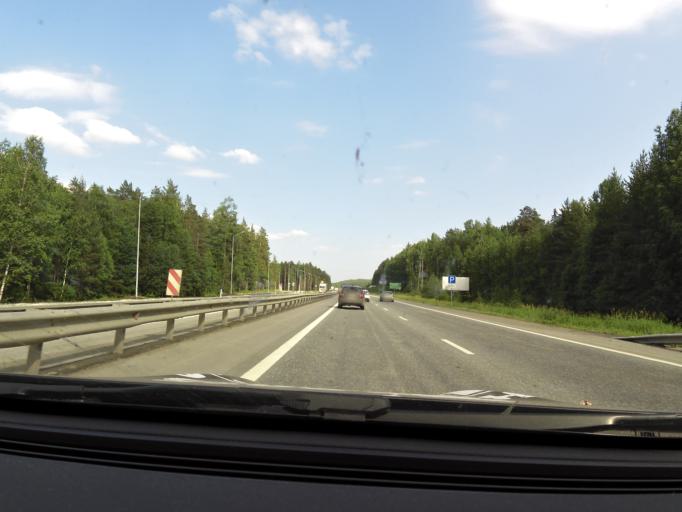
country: RU
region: Sverdlovsk
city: Severka
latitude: 56.8401
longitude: 60.2630
